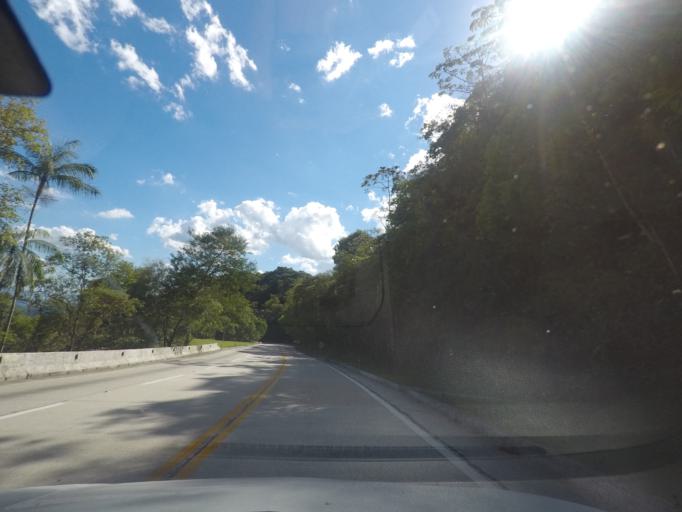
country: BR
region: Rio de Janeiro
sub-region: Guapimirim
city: Guapimirim
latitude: -22.4851
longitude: -42.9962
